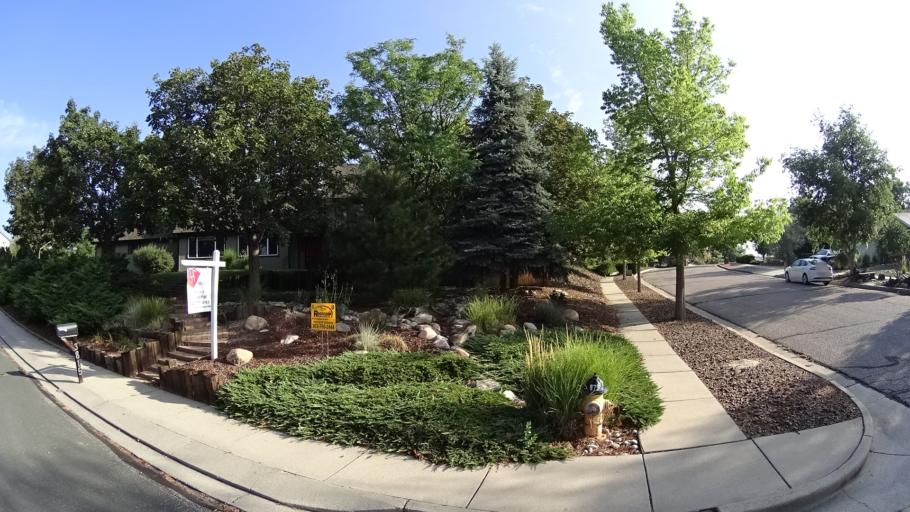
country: US
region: Colorado
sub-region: El Paso County
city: Colorado Springs
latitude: 38.8865
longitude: -104.7928
